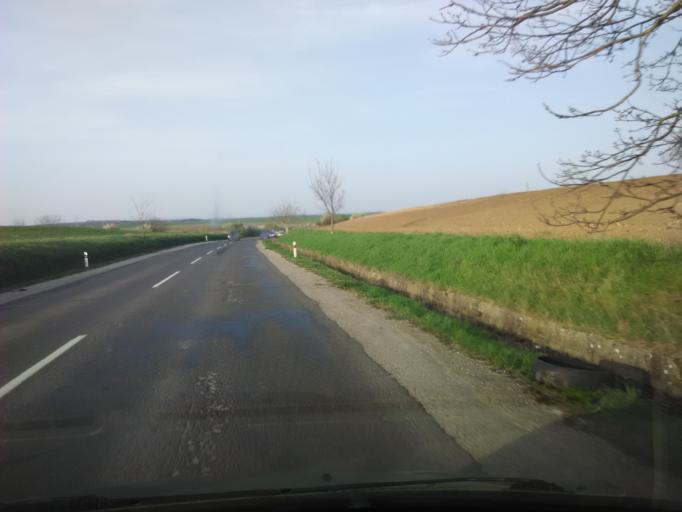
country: SK
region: Nitriansky
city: Surany
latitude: 48.0961
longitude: 18.2943
